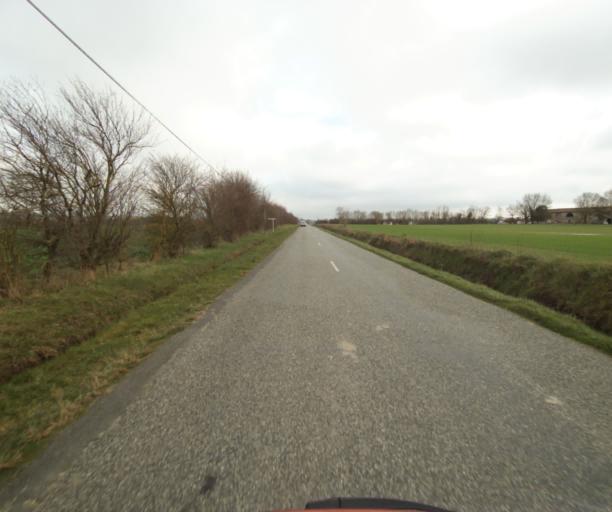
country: FR
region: Languedoc-Roussillon
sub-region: Departement de l'Aude
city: Belpech
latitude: 43.2179
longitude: 1.7141
